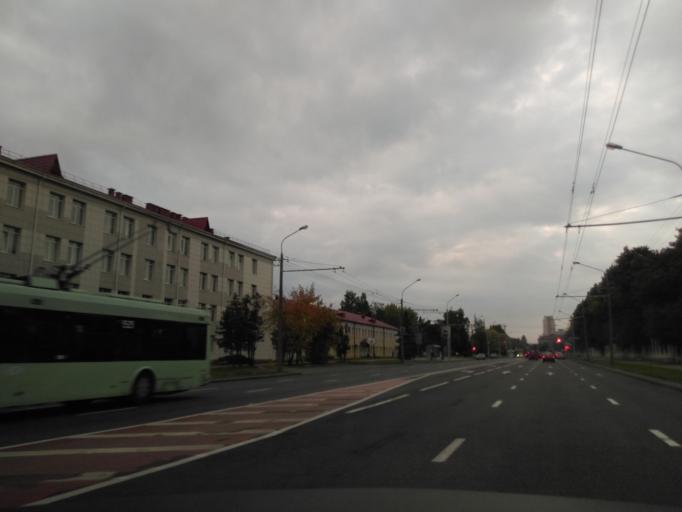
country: BY
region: Minsk
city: Minsk
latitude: 53.9089
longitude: 27.6114
